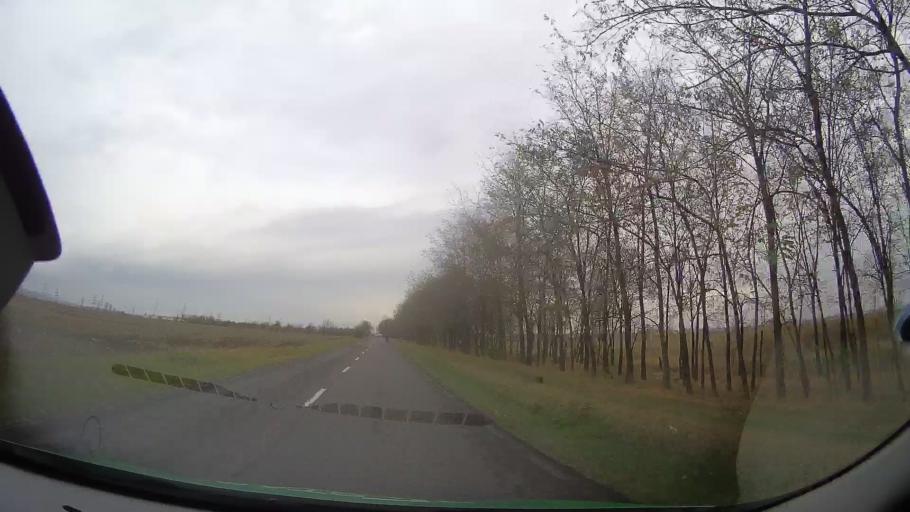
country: RO
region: Prahova
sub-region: Comuna Berceni
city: Berceni
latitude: 44.9395
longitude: 26.1089
